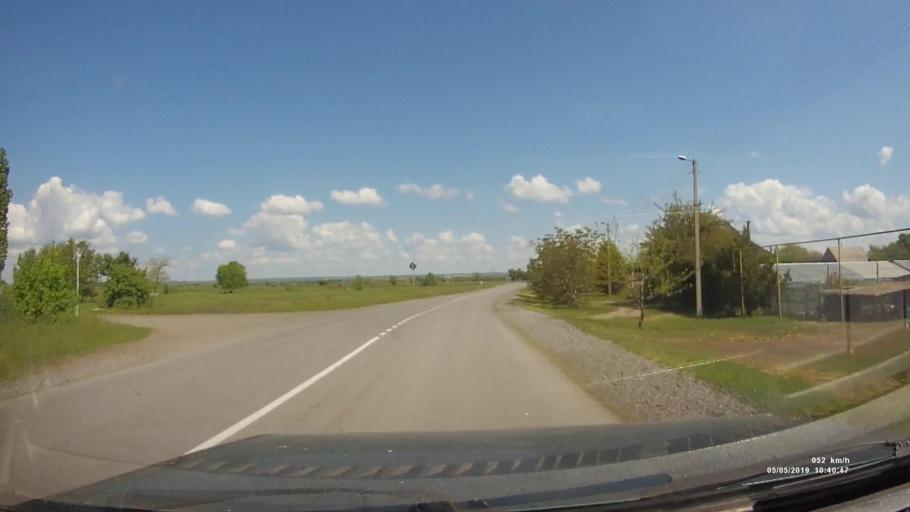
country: RU
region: Rostov
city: Ust'-Donetskiy
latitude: 47.5867
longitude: 40.8421
